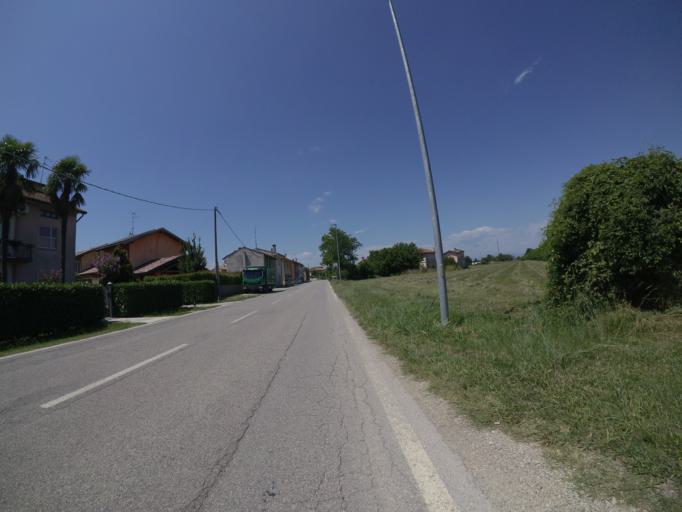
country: IT
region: Friuli Venezia Giulia
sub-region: Provincia di Udine
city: Talmassons
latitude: 45.9268
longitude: 13.1275
